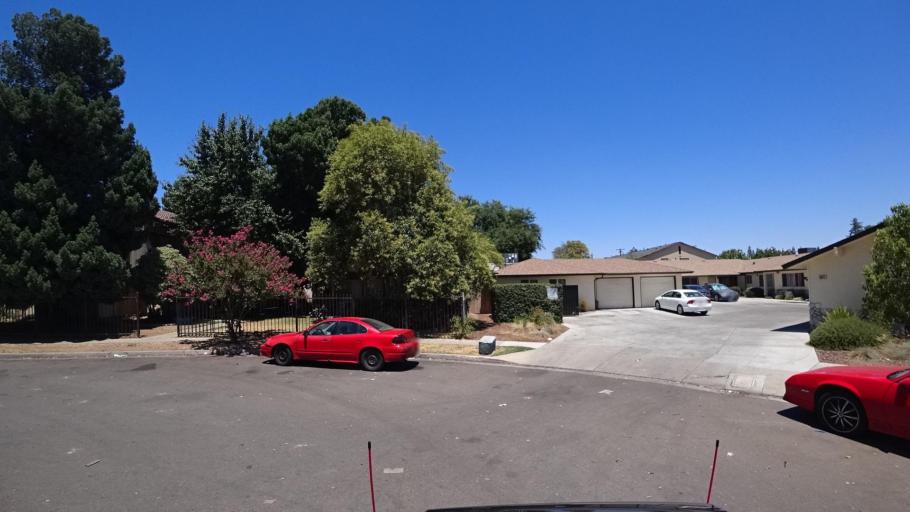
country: US
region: California
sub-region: Fresno County
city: Sunnyside
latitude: 36.7331
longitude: -119.7256
